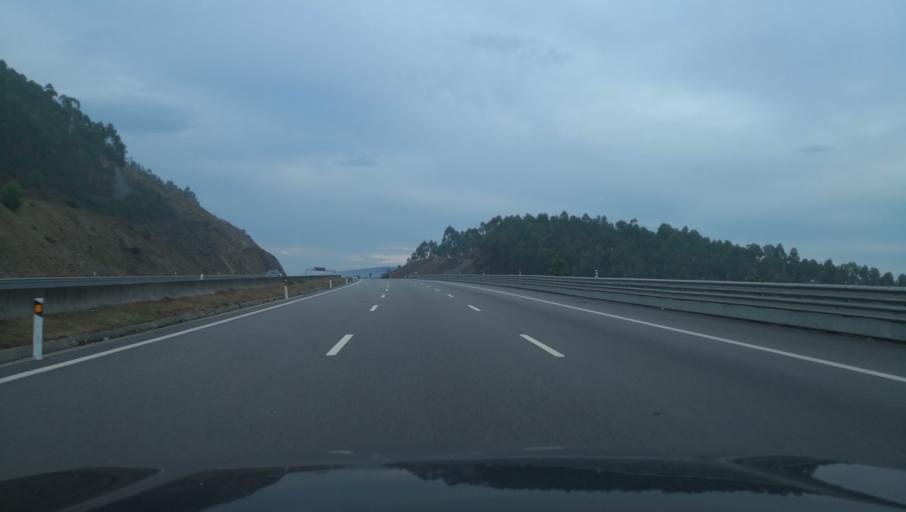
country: PT
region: Porto
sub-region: Paredes
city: Recarei
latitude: 41.1225
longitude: -8.4334
